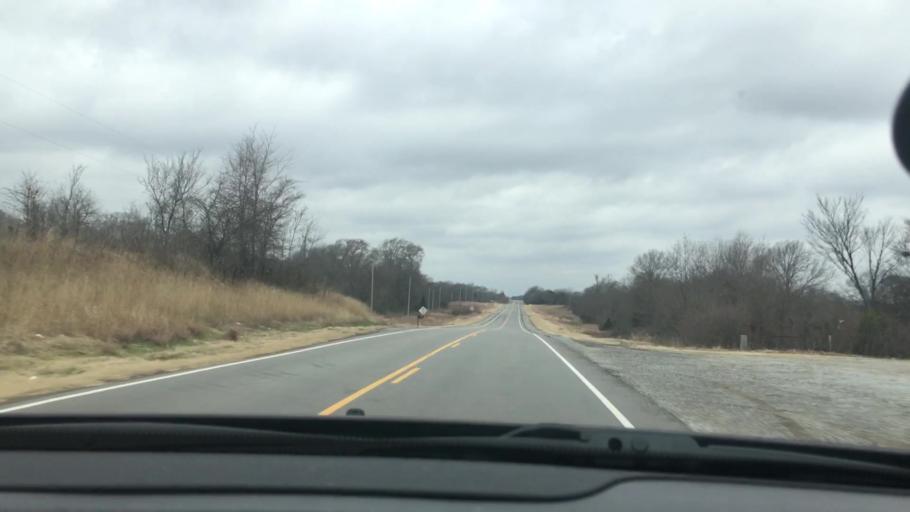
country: US
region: Oklahoma
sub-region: Atoka County
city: Atoka
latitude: 34.3749
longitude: -96.1537
